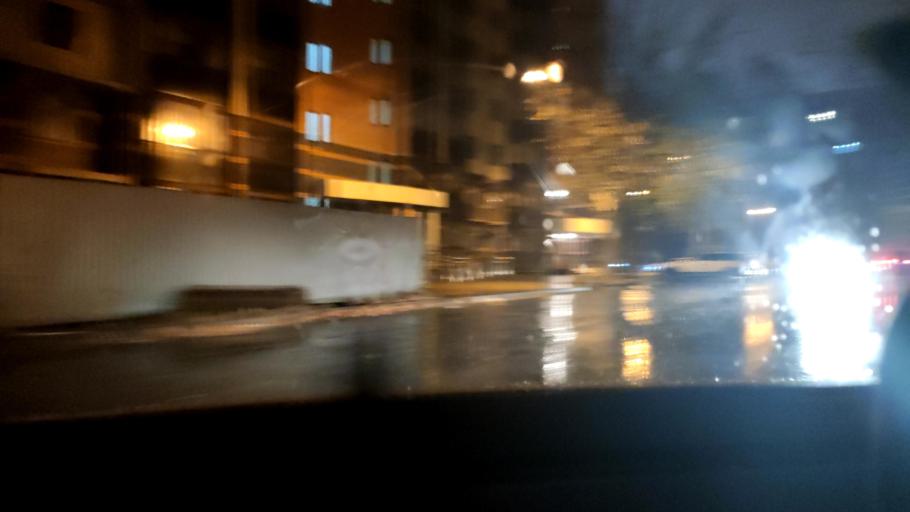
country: RU
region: Voronezj
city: Voronezh
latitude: 51.7044
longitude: 39.1879
